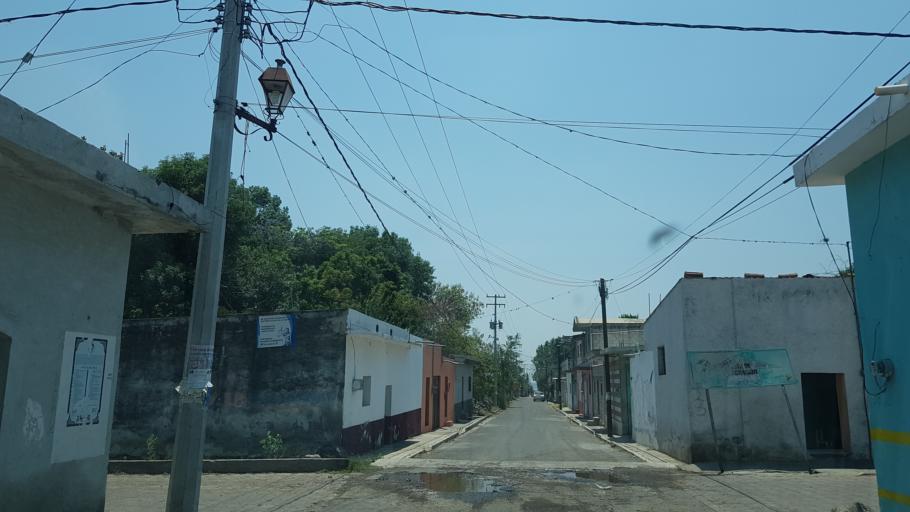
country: MX
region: Puebla
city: Huaquechula
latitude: 18.7747
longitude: -98.5454
